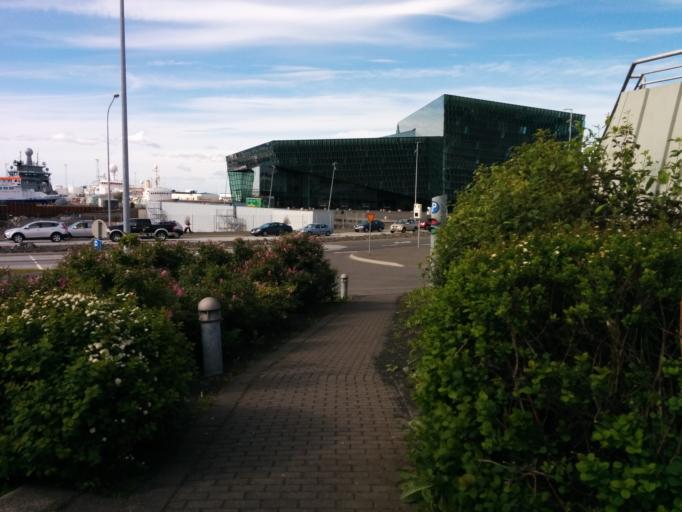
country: IS
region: Capital Region
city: Reykjavik
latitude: 64.1484
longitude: -21.9335
